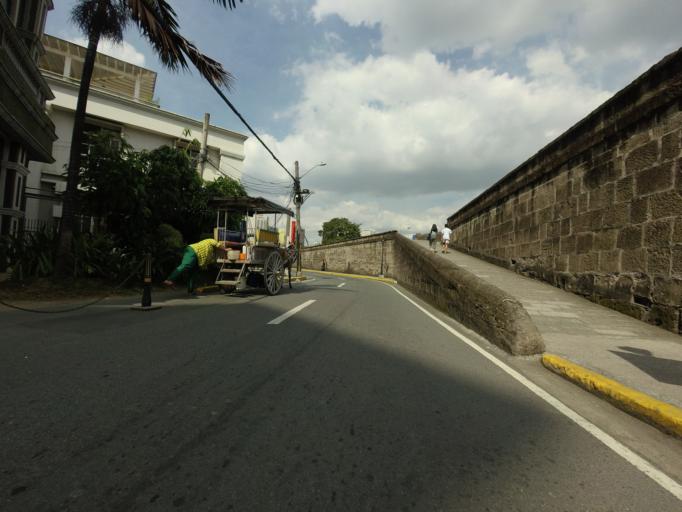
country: PH
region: Metro Manila
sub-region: City of Manila
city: Quiapo
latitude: 14.5902
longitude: 120.9790
